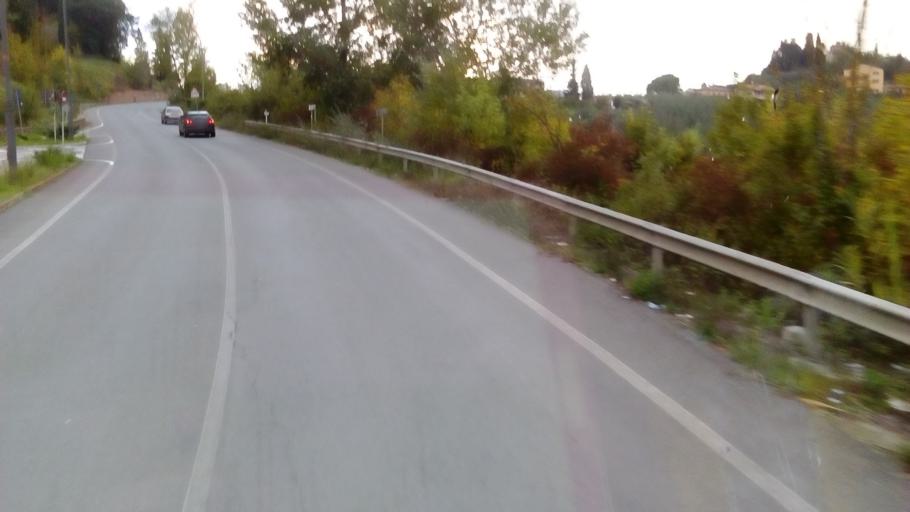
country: IT
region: Tuscany
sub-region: Province of Florence
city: Castelfiorentino
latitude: 43.6063
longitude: 10.9756
